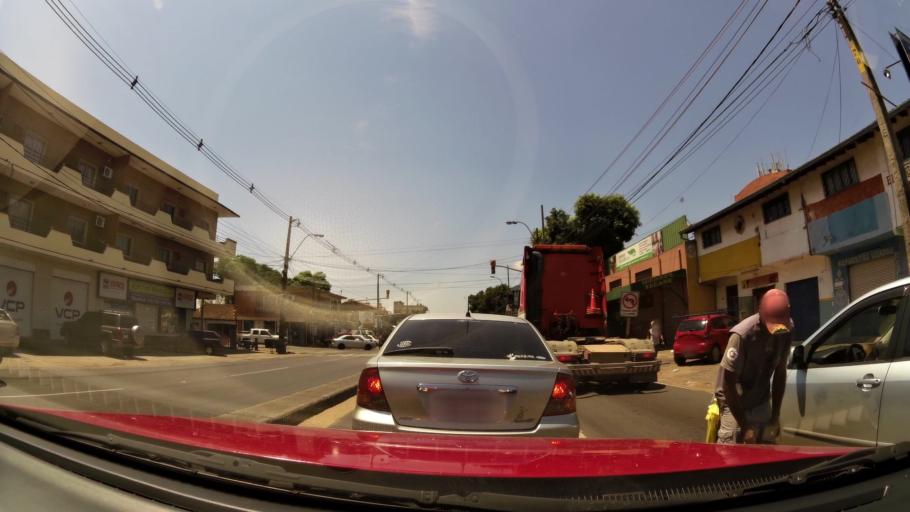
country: PY
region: Central
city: Fernando de la Mora
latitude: -25.3244
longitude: -57.5657
